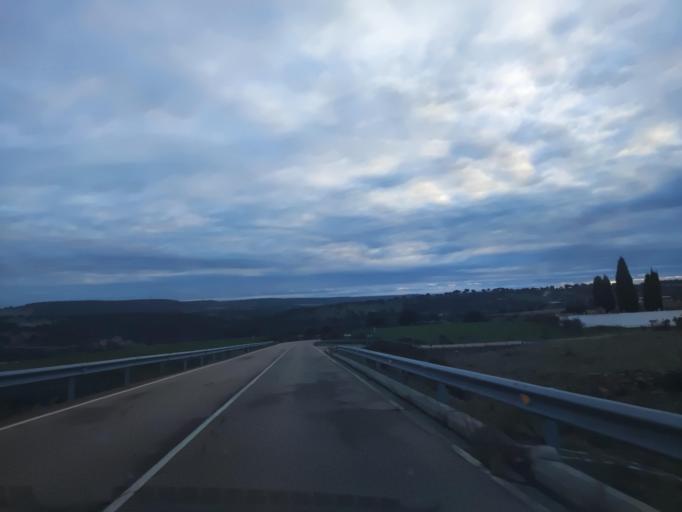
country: ES
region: Castille and Leon
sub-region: Provincia de Salamanca
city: Castillejo de Martin Viejo
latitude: 40.7059
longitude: -6.6456
